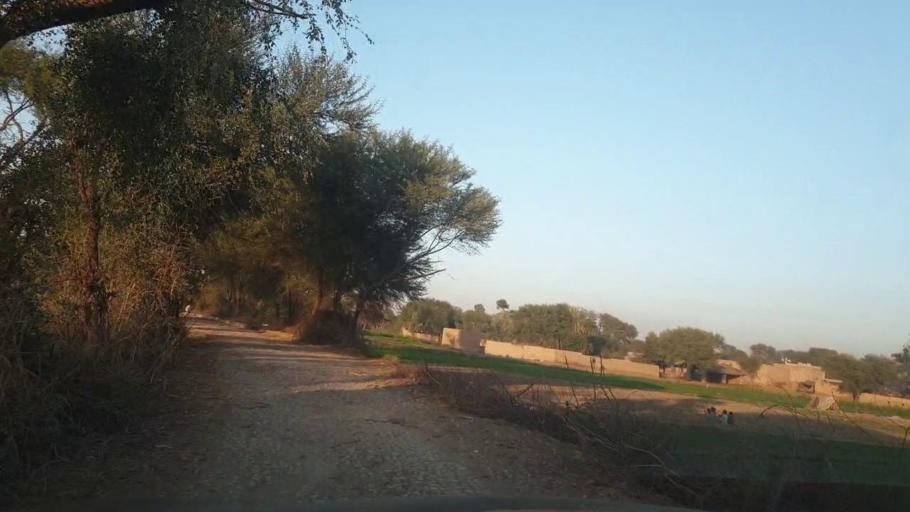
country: PK
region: Sindh
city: Ubauro
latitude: 28.1780
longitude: 69.6041
